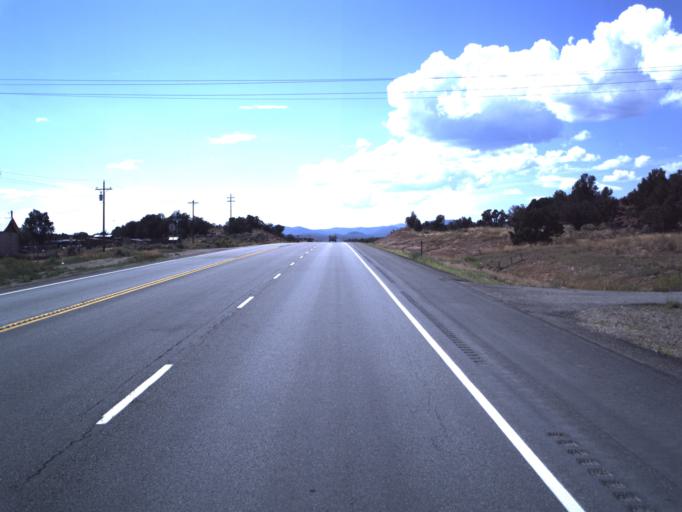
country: US
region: Utah
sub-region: Duchesne County
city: Duchesne
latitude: 40.2038
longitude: -110.7949
